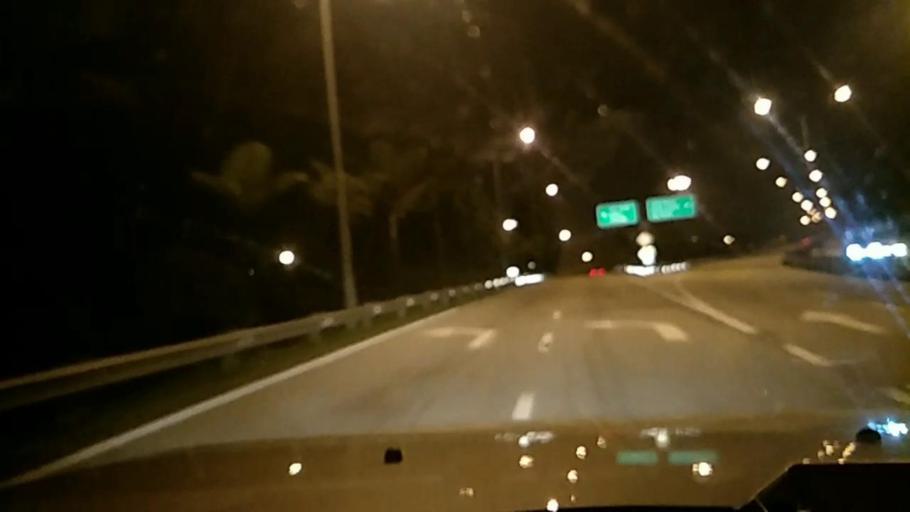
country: MY
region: Selangor
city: Kuang
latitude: 3.2796
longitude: 101.5535
